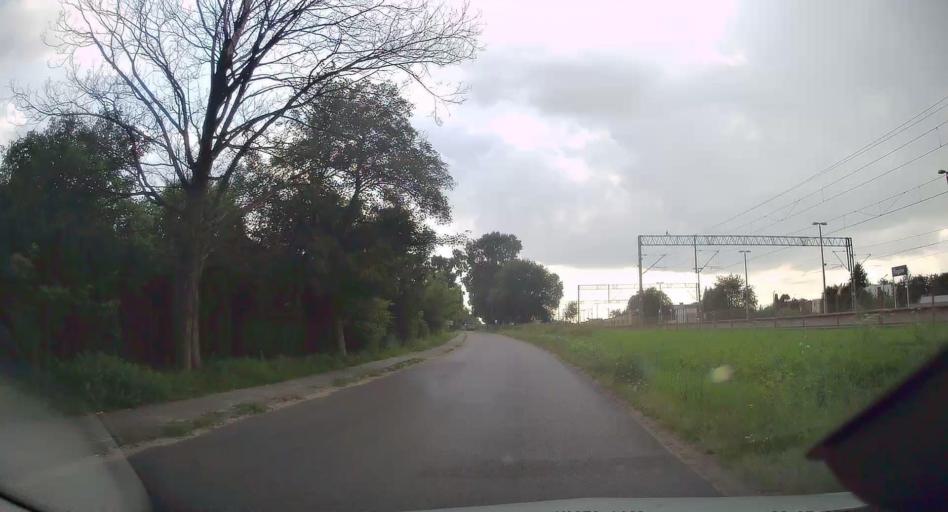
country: PL
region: Lodz Voivodeship
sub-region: Powiat brzezinski
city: Rogow
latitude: 51.8194
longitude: 19.8884
